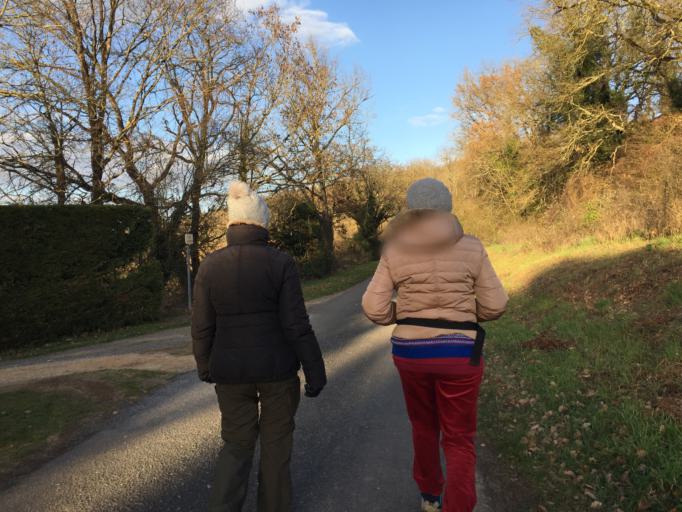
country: FR
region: Poitou-Charentes
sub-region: Departement de la Vienne
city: Chauvigny
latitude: 46.5195
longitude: 0.6469
